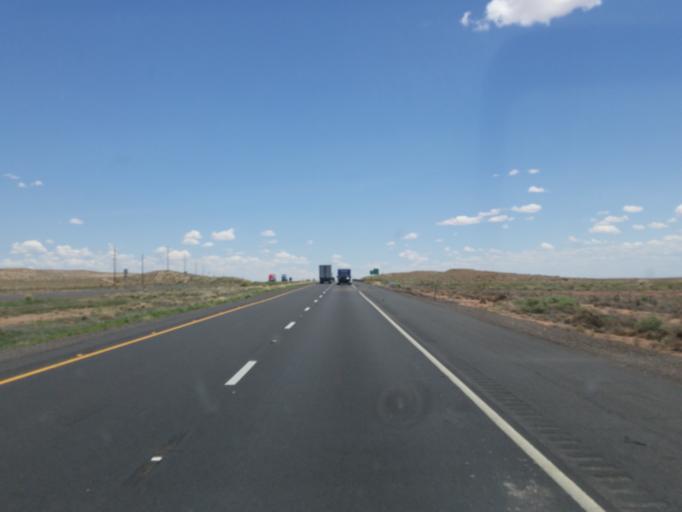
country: US
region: Arizona
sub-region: Navajo County
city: Winslow
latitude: 34.9784
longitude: -110.5356
